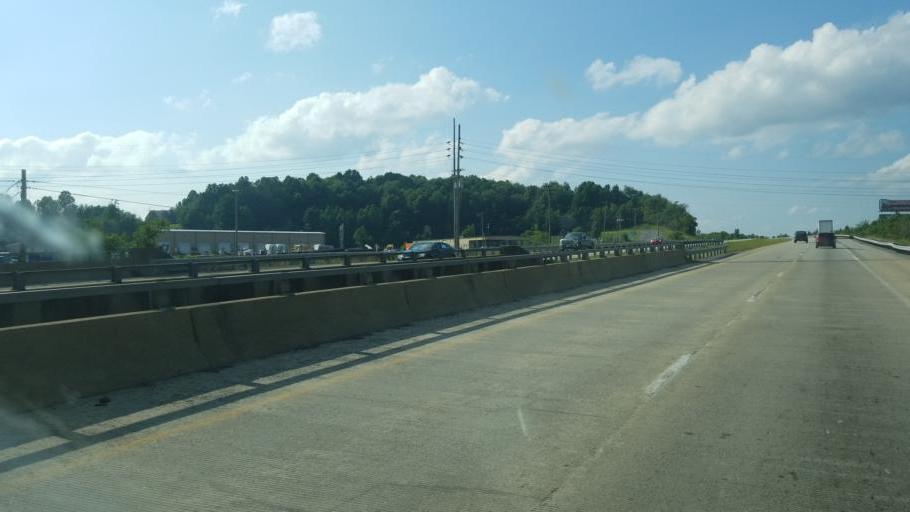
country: US
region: West Virginia
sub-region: Monongalia County
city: Star City
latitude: 39.6924
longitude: -80.0425
